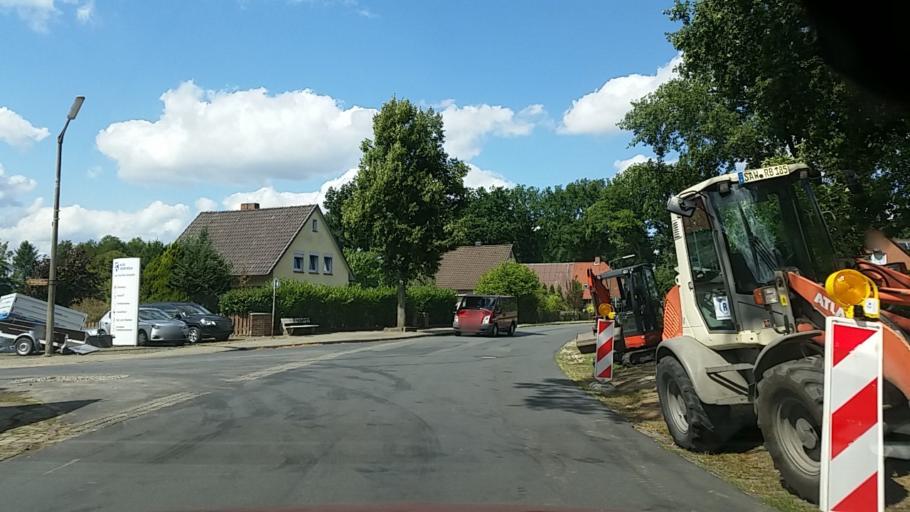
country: DE
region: Lower Saxony
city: Hankensbuttel
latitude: 52.7101
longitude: 10.6261
